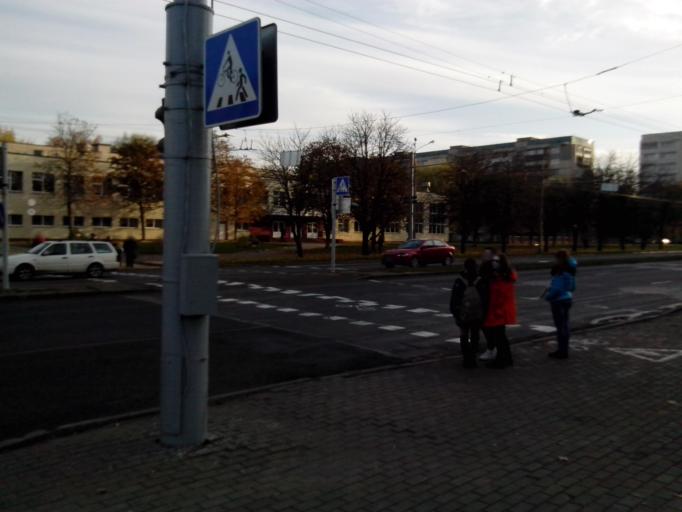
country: BY
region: Minsk
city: Minsk
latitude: 53.9262
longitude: 27.5716
